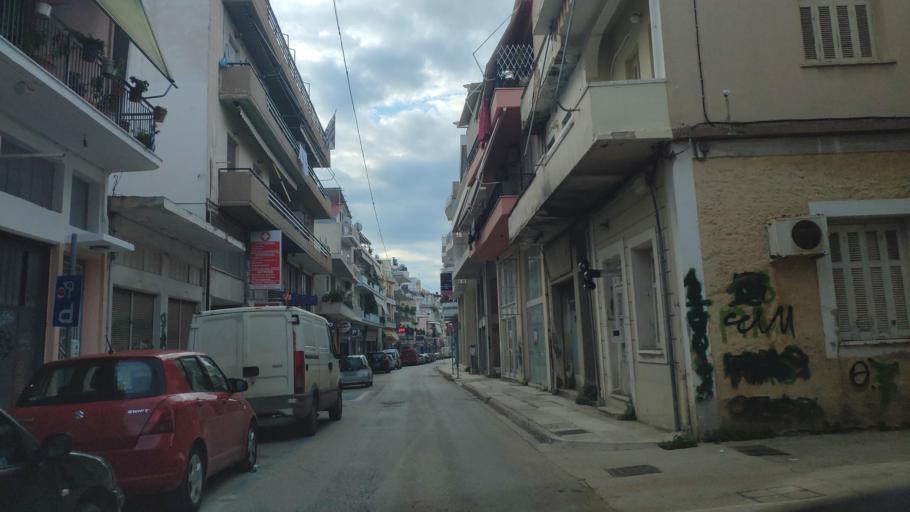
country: GR
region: Peloponnese
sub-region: Nomos Argolidos
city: Argos
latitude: 37.6386
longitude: 22.7289
